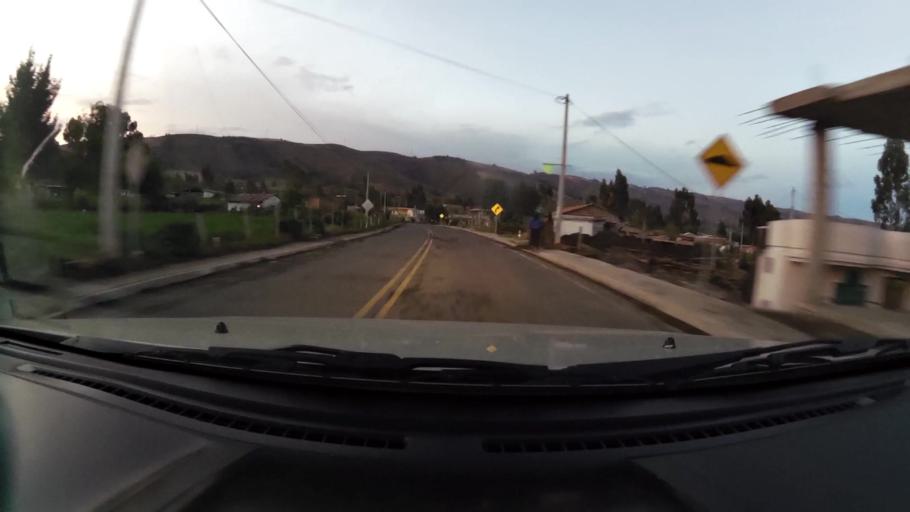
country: EC
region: Chimborazo
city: Riobamba
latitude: -1.9063
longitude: -78.6967
